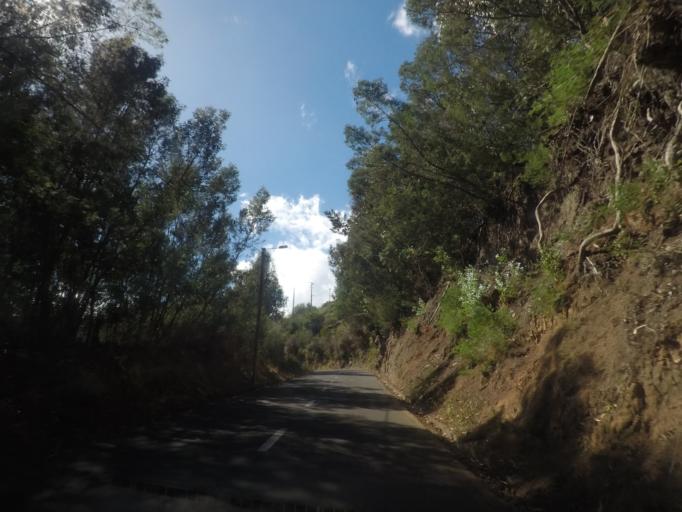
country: PT
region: Madeira
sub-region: Ribeira Brava
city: Campanario
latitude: 32.6940
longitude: -17.0313
